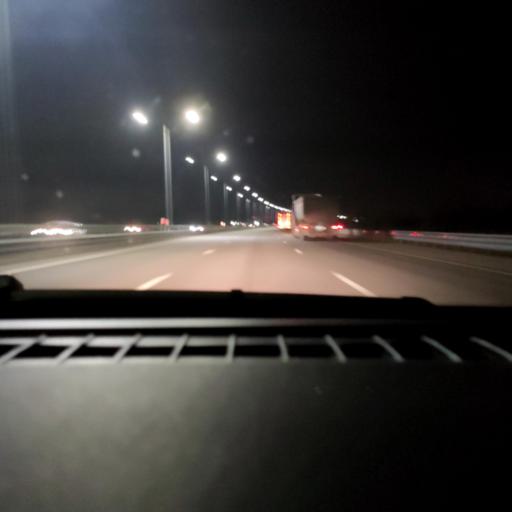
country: RU
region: Voronezj
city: Somovo
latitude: 51.7644
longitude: 39.3057
